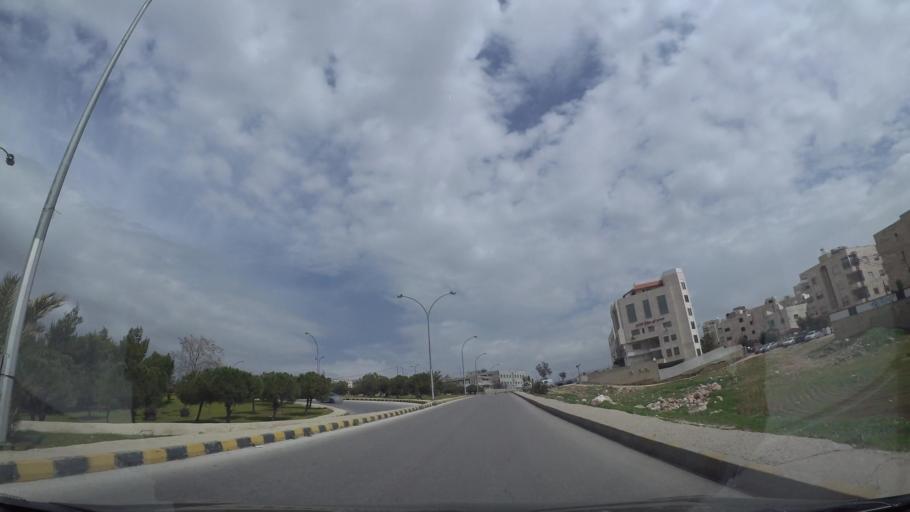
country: JO
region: Amman
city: Amman
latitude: 31.9924
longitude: 35.9190
